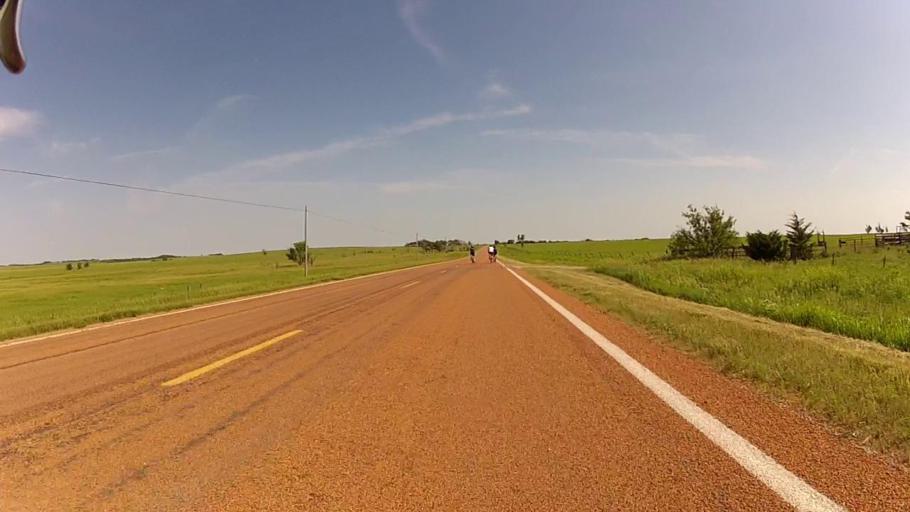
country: US
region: Kansas
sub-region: Cowley County
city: Winfield
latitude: 37.0745
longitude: -96.6436
